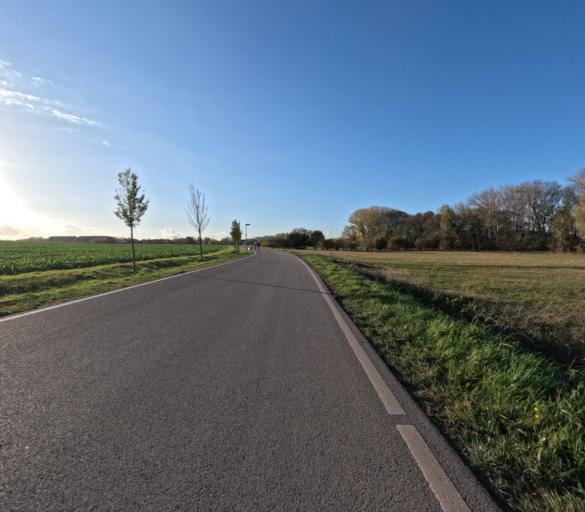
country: DE
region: Saxony-Anhalt
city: Gunthersdorf
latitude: 51.3566
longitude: 12.1813
